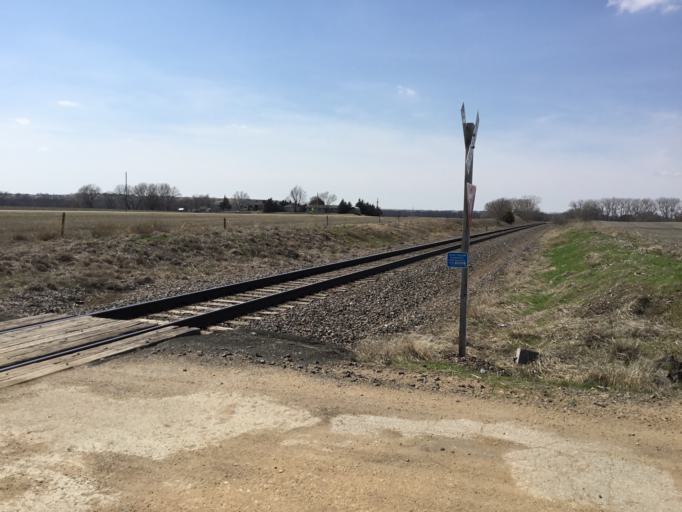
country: US
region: Kansas
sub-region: Ellsworth County
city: Ellsworth
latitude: 38.7113
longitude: -98.1882
